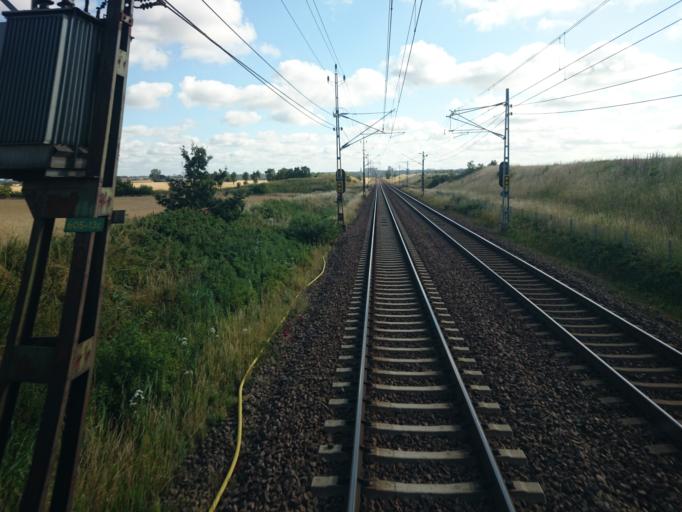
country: SE
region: Skane
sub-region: Staffanstorps Kommun
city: Hjaerup
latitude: 55.6769
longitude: 13.1413
